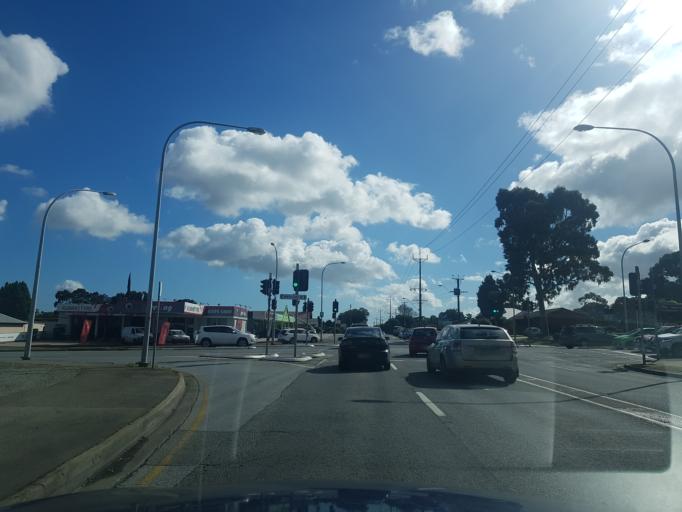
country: AU
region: South Australia
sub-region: Tea Tree Gully
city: Hope Valley
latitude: -34.8215
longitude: 138.7187
